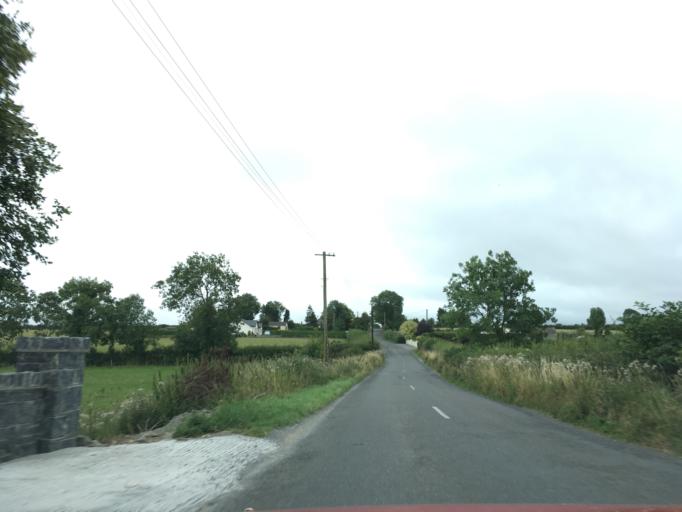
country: IE
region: Munster
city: Cashel
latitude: 52.4744
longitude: -7.8673
